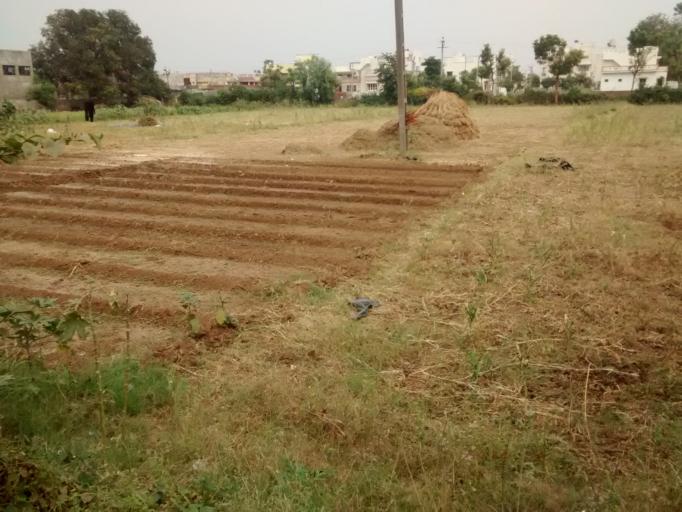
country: IN
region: Gujarat
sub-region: Gandhinagar
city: Dahegam
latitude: 23.1599
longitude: 72.8076
